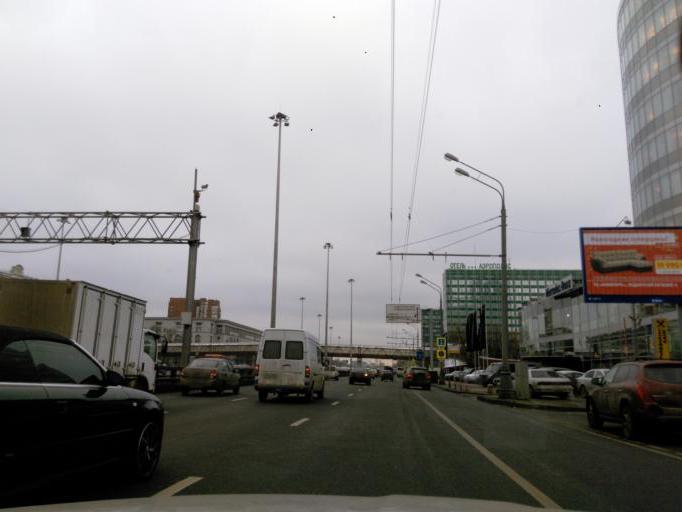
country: RU
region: Moscow
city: Sokol
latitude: 55.7963
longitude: 37.5404
